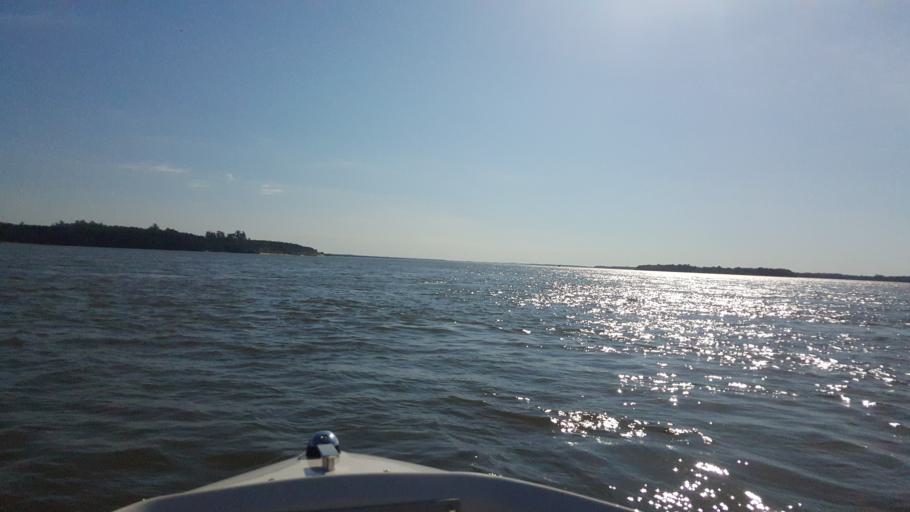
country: AR
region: Corrientes
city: Ituzaingo
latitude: -27.6037
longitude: -56.8493
